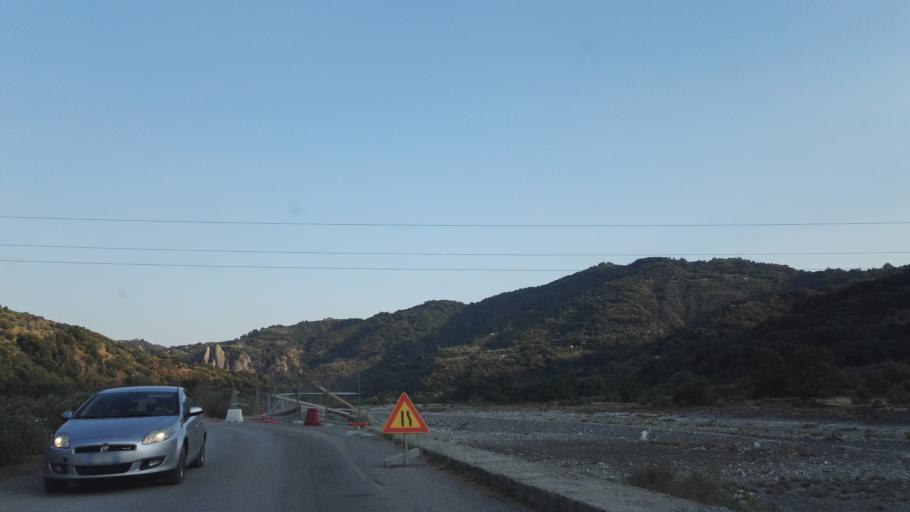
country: IT
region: Calabria
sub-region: Provincia di Reggio Calabria
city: Caulonia
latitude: 38.4159
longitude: 16.3805
